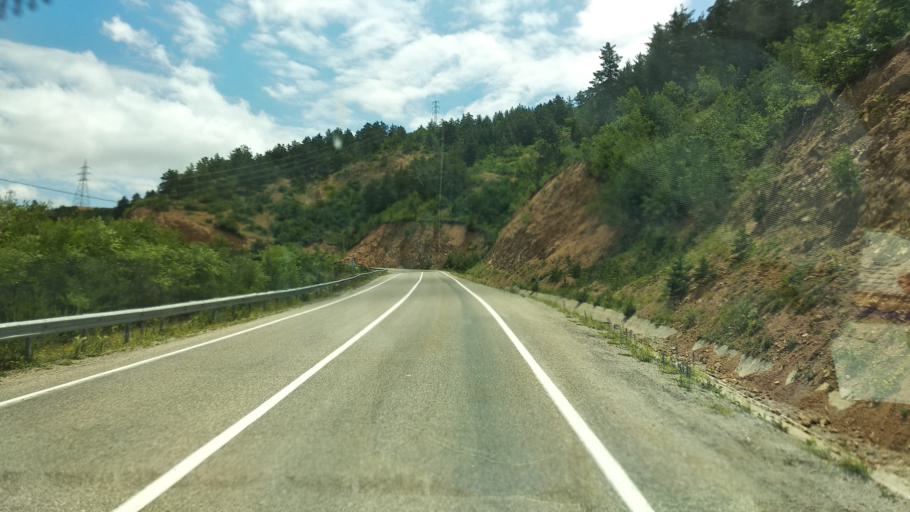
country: TR
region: Gumushane
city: Kose
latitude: 40.2990
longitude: 39.5655
